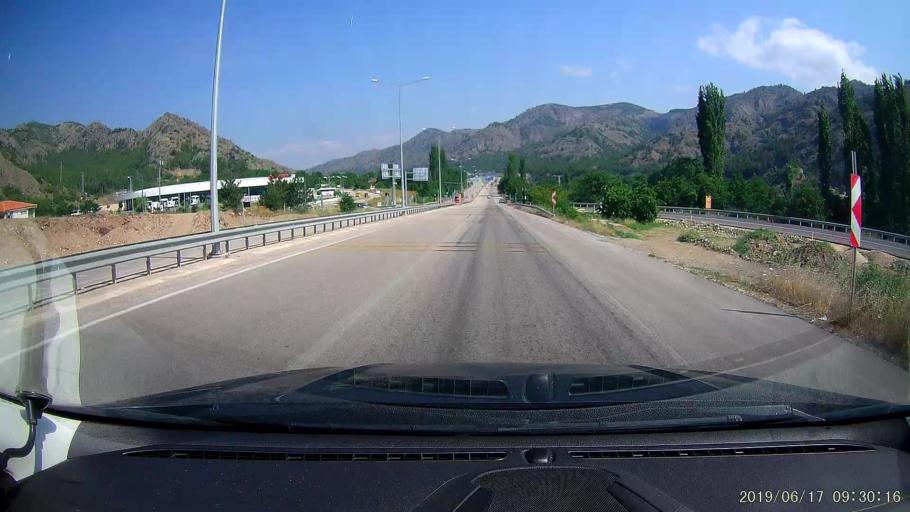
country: TR
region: Amasya
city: Amasya
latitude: 40.7043
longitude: 35.8049
